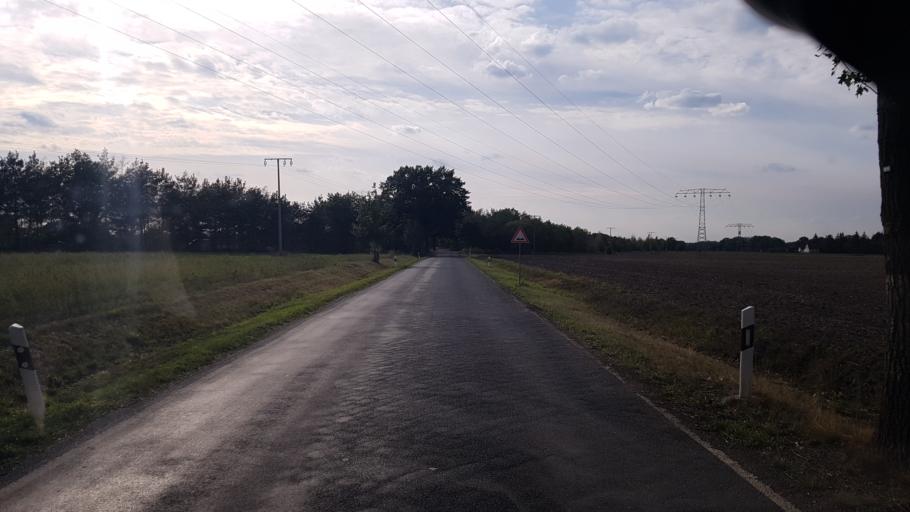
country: DE
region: Brandenburg
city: Welzow
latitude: 51.5566
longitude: 14.1421
